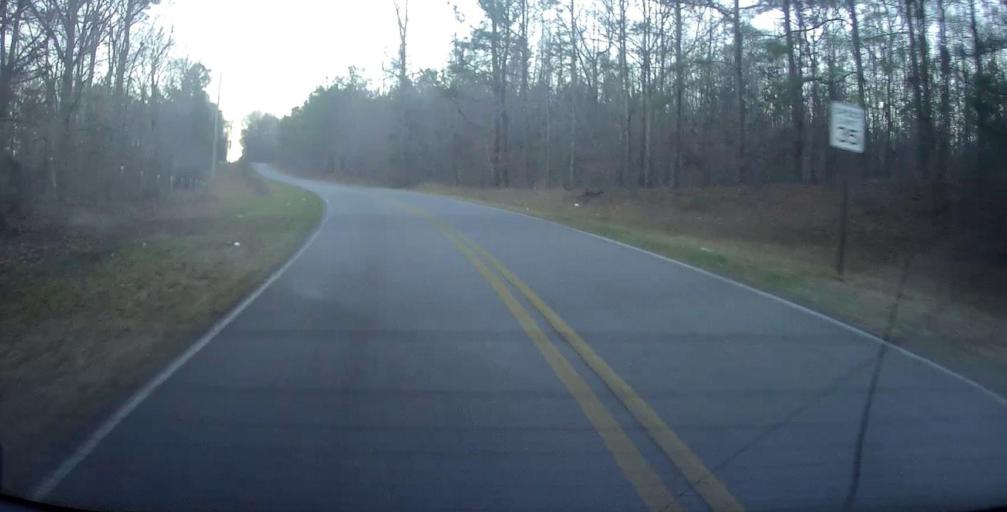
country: US
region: Georgia
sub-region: Troup County
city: La Grange
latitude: 33.0507
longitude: -84.9697
